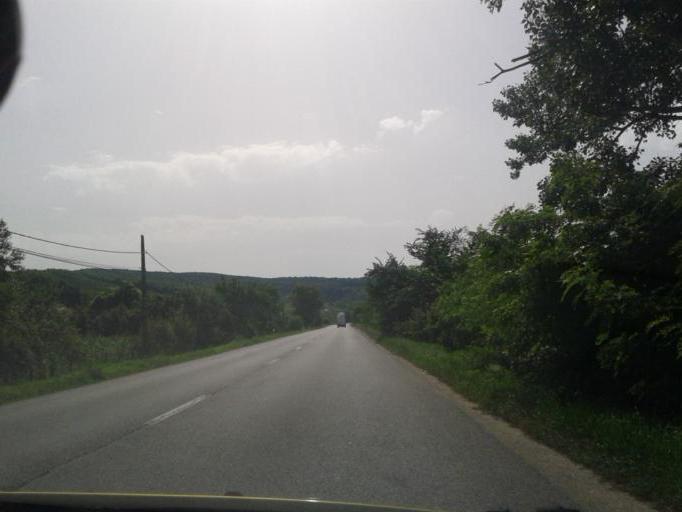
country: RO
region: Valcea
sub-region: Comuna Mihaesti
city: Mihaesti
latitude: 45.0635
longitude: 24.2369
